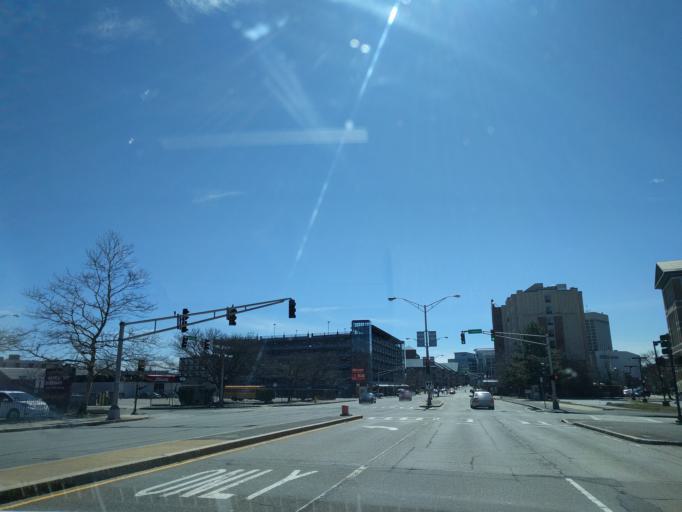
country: US
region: Massachusetts
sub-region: Worcester County
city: Worcester
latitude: 42.2703
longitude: -71.7989
